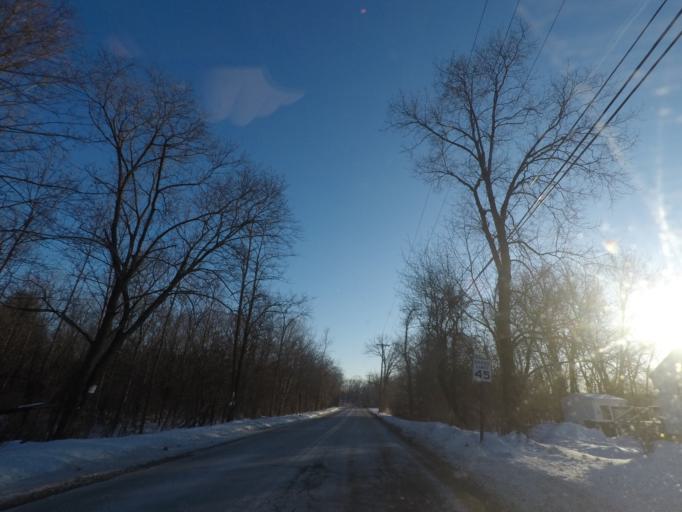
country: US
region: New York
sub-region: Saratoga County
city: Mechanicville
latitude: 42.8982
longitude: -73.6788
